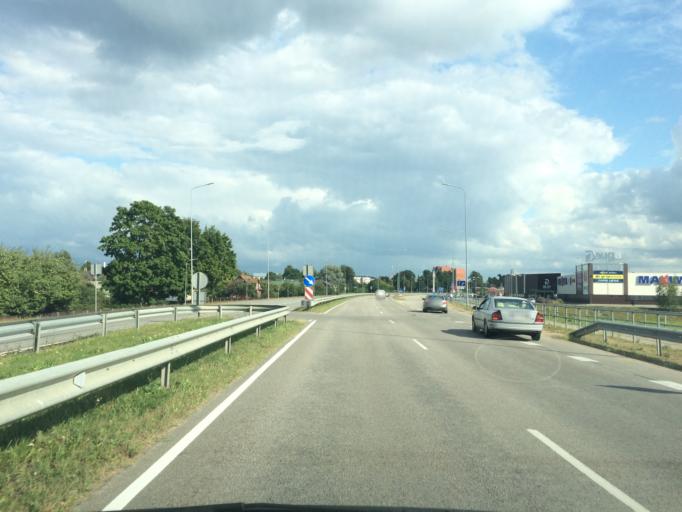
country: LV
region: Ogre
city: Ogre
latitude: 56.8179
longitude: 24.5817
